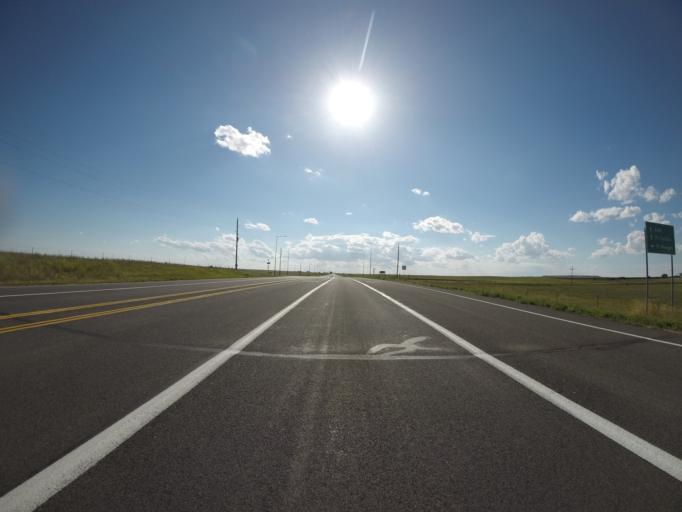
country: US
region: Colorado
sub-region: Morgan County
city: Fort Morgan
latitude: 40.6114
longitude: -103.8005
